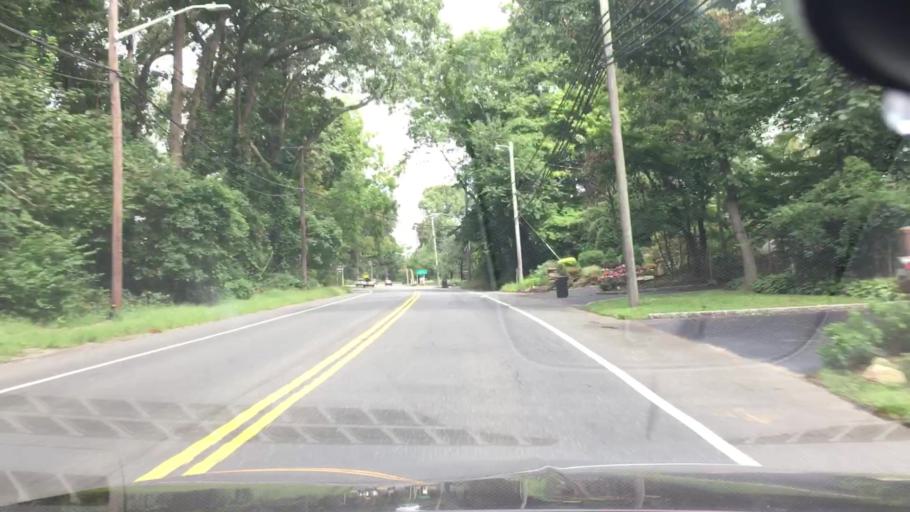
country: US
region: New York
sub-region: Suffolk County
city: Head of the Harbor
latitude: 40.8932
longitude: -73.1542
